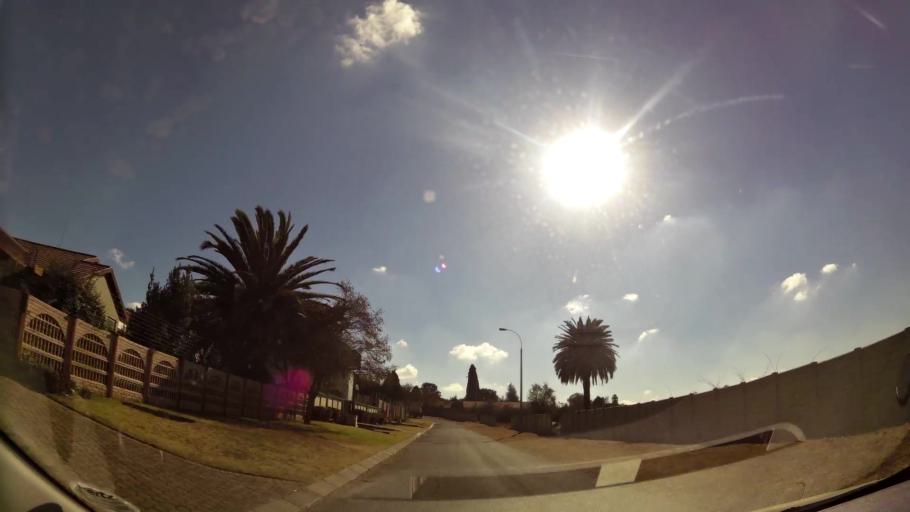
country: ZA
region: Gauteng
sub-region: City of Johannesburg Metropolitan Municipality
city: Roodepoort
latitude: -26.1495
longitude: 27.8370
